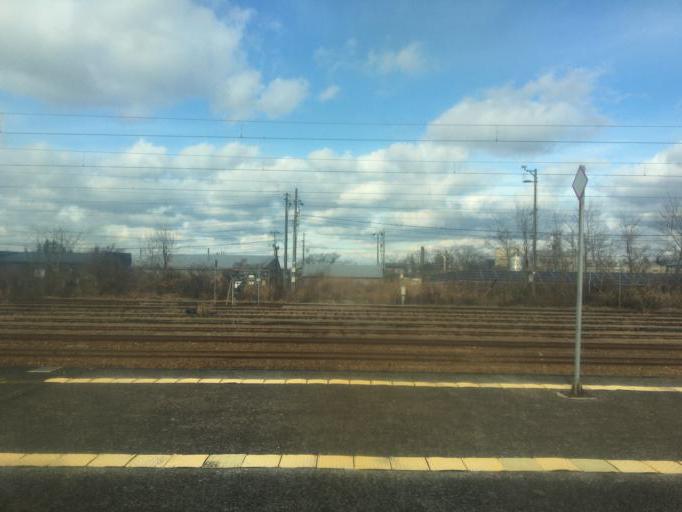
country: JP
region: Akita
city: Noshiromachi
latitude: 40.1921
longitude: 140.0671
